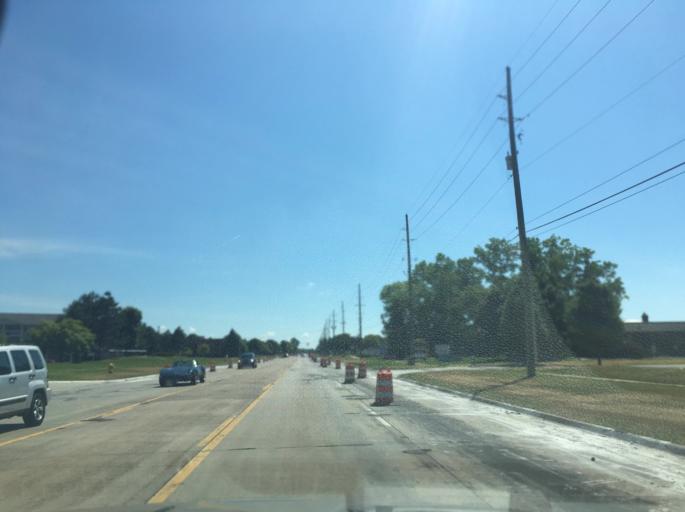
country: US
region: Michigan
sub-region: Macomb County
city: Clinton
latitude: 42.6125
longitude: -82.9666
